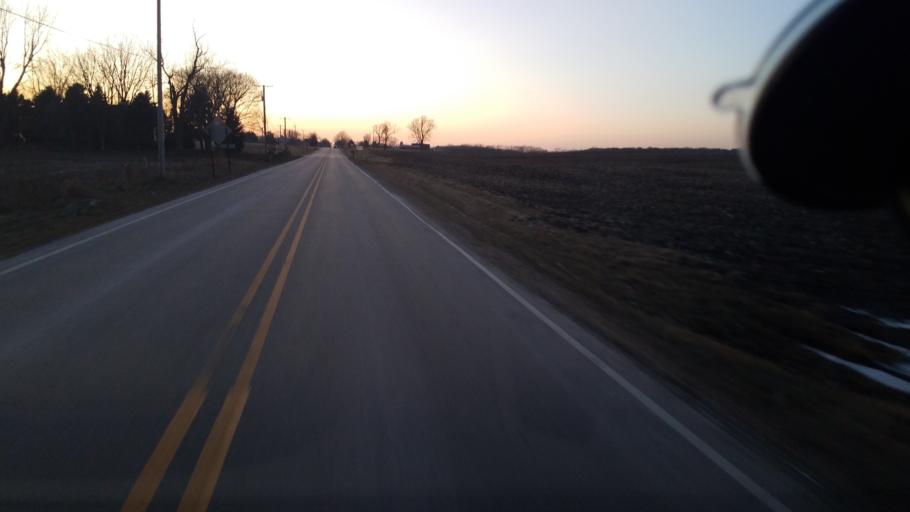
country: US
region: Illinois
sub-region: Kane County
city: Hampshire
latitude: 42.1609
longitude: -88.5305
